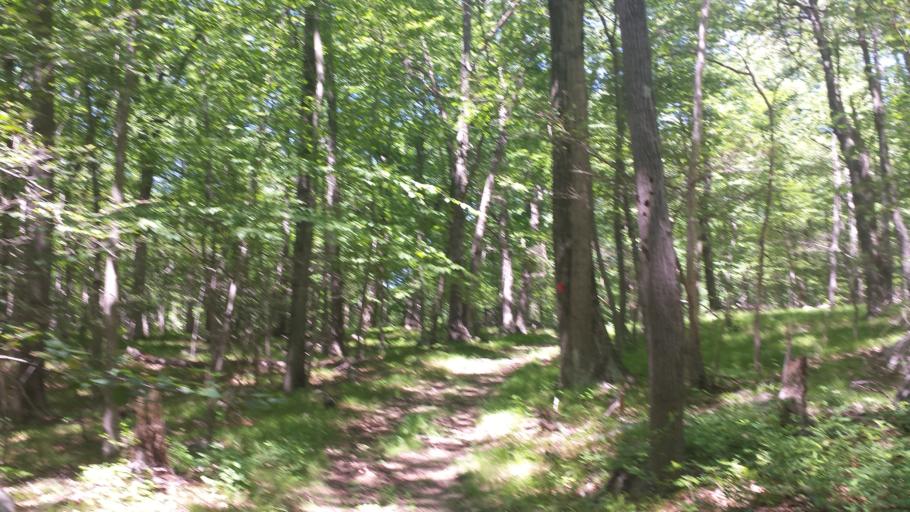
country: US
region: New York
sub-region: Westchester County
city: Pound Ridge
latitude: 41.2365
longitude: -73.5802
